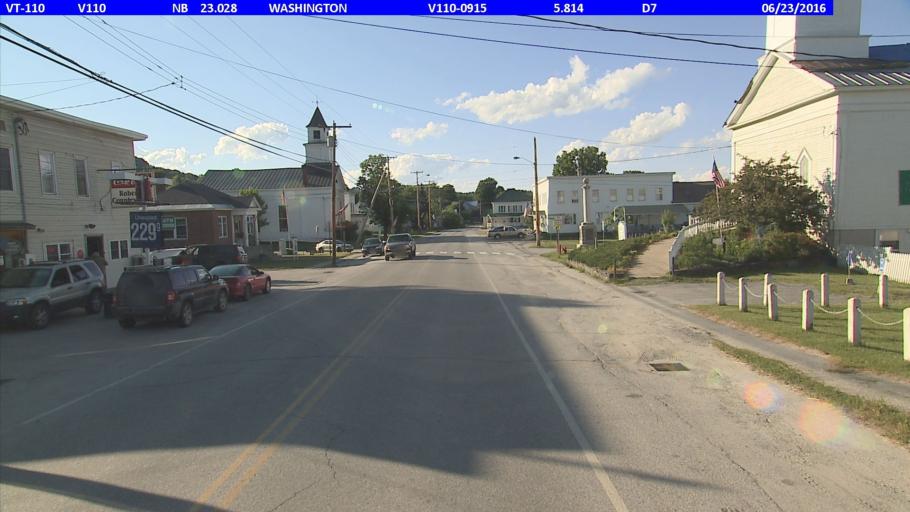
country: US
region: Vermont
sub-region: Washington County
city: South Barre
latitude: 44.1072
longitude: -72.4332
